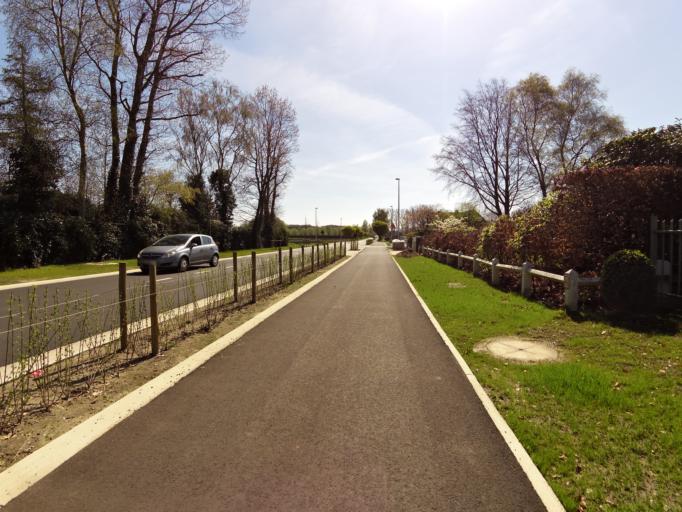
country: BE
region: Flanders
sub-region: Provincie West-Vlaanderen
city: Jabbeke
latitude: 51.1749
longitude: 3.0874
